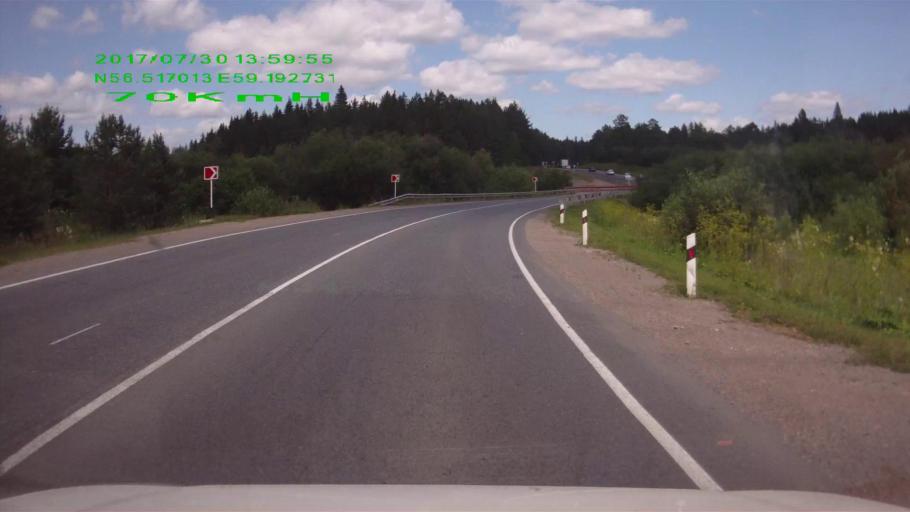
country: RU
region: Sverdlovsk
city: Mikhaylovsk
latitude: 56.5173
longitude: 59.1928
